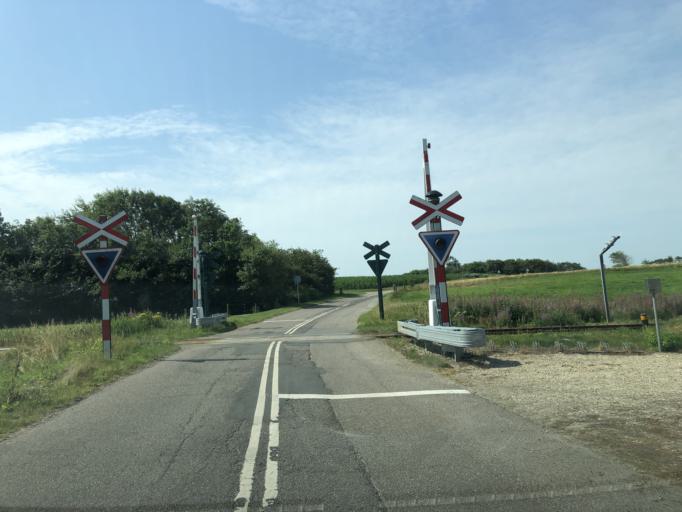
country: DK
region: Central Jutland
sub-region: Lemvig Kommune
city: Lemvig
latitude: 56.4378
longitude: 8.2845
